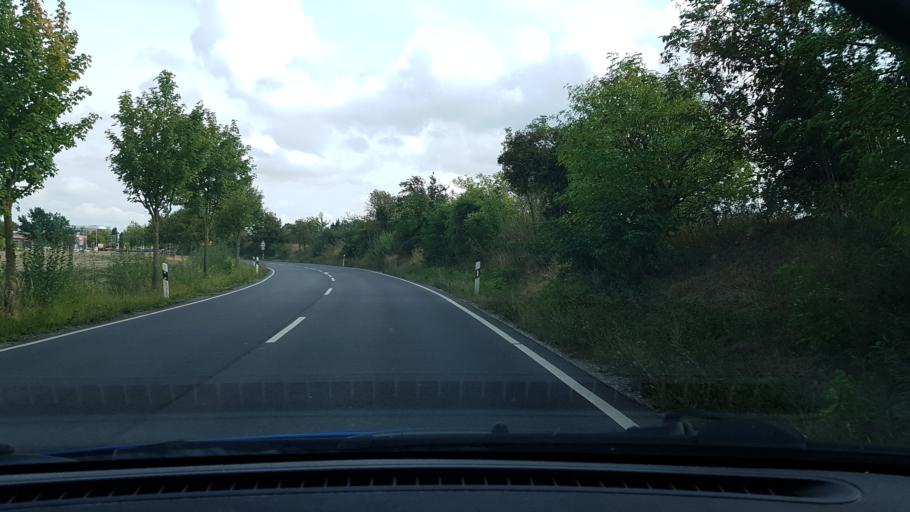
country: DE
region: Lower Saxony
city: Grossgoltern
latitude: 52.3097
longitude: 9.4848
